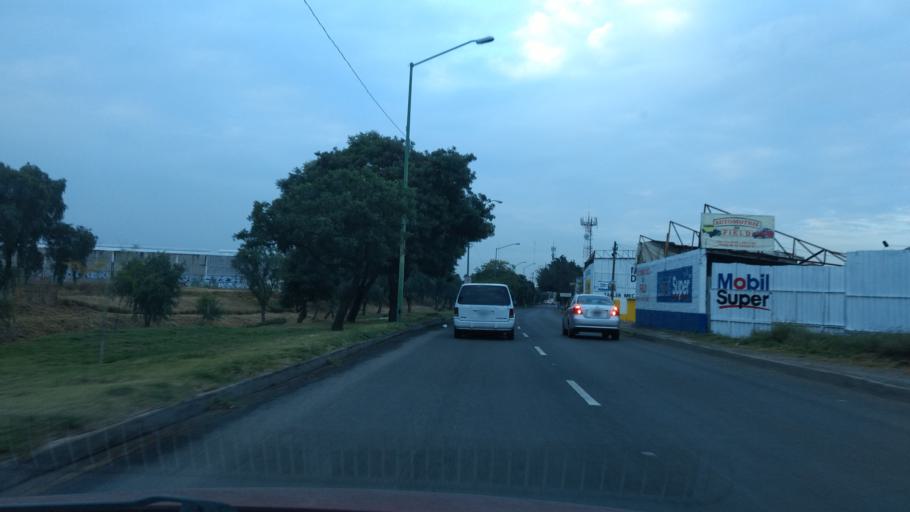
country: MX
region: Guanajuato
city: Leon
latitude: 21.1012
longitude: -101.6626
